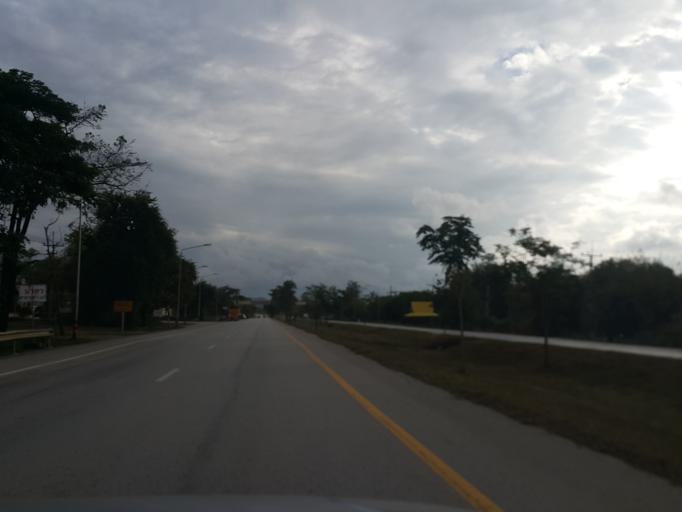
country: TH
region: Lampang
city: Ko Kha
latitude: 18.1666
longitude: 99.4057
